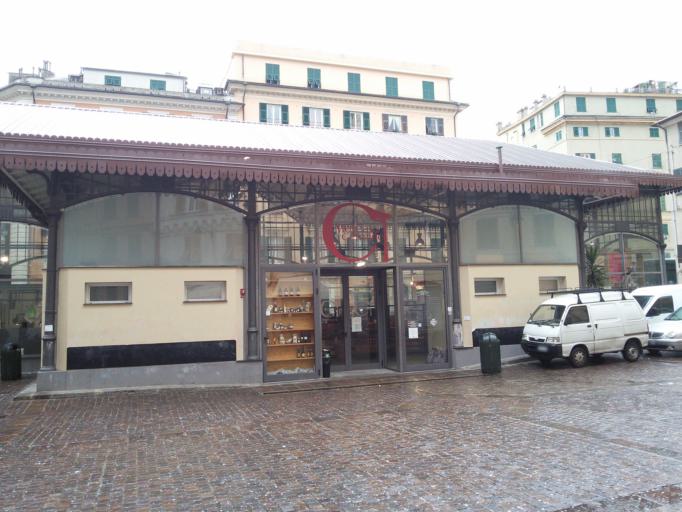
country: IT
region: Liguria
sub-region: Provincia di Genova
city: Genoa
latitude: 44.4151
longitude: 8.9298
